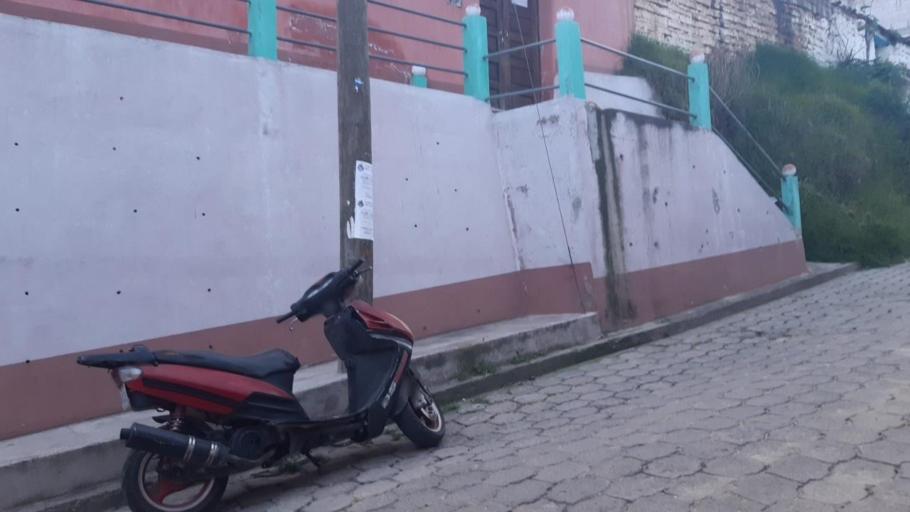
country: GT
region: Quetzaltenango
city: Salcaja
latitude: 14.8833
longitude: -91.4613
